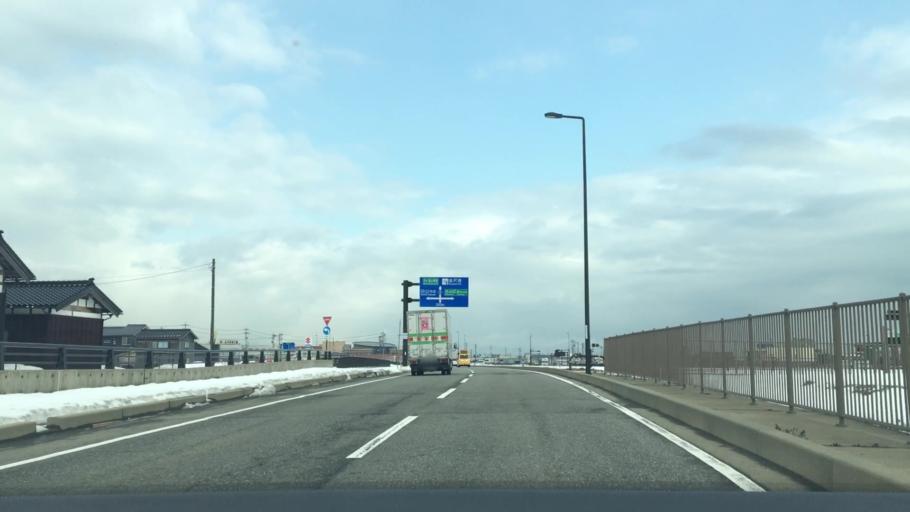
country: JP
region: Ishikawa
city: Matsuto
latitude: 36.5544
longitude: 136.5799
